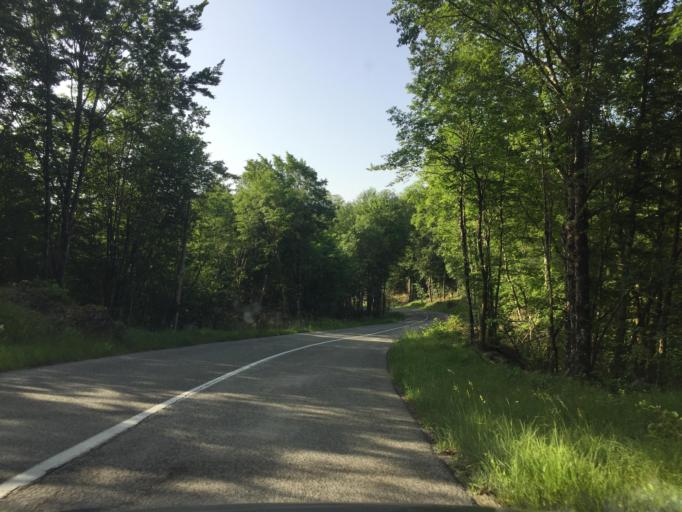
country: HR
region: Primorsko-Goranska
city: Matulji
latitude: 45.4111
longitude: 14.2503
